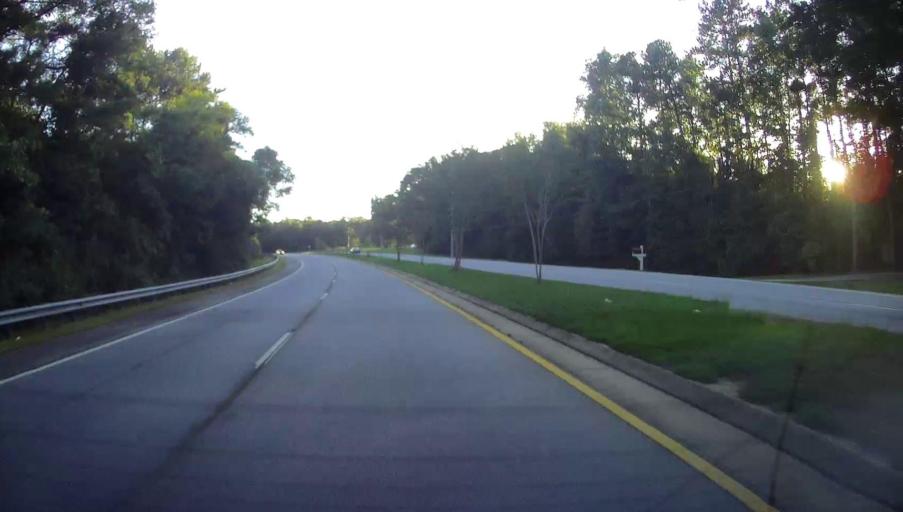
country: US
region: Georgia
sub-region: Muscogee County
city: Columbus
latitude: 32.5351
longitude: -84.8500
